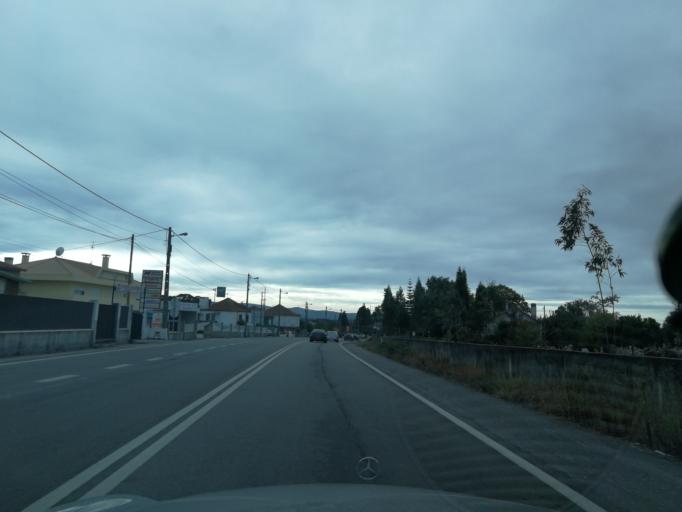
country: PT
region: Aveiro
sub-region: Agueda
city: Agueda
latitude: 40.5891
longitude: -8.4509
